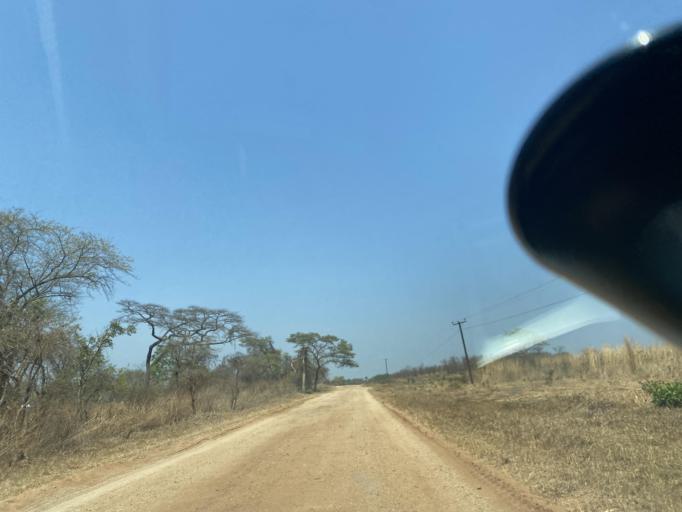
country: ZM
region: Lusaka
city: Lusaka
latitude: -15.5408
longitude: 28.0768
